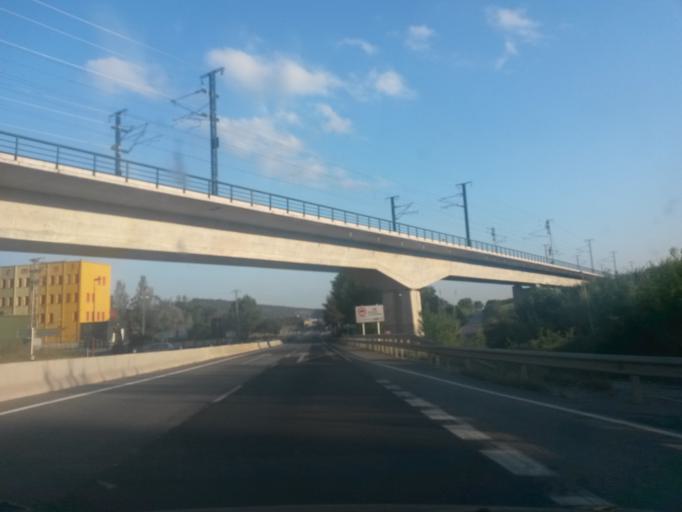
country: ES
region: Catalonia
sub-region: Provincia de Girona
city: Sarria de Ter
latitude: 42.0405
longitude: 2.8221
